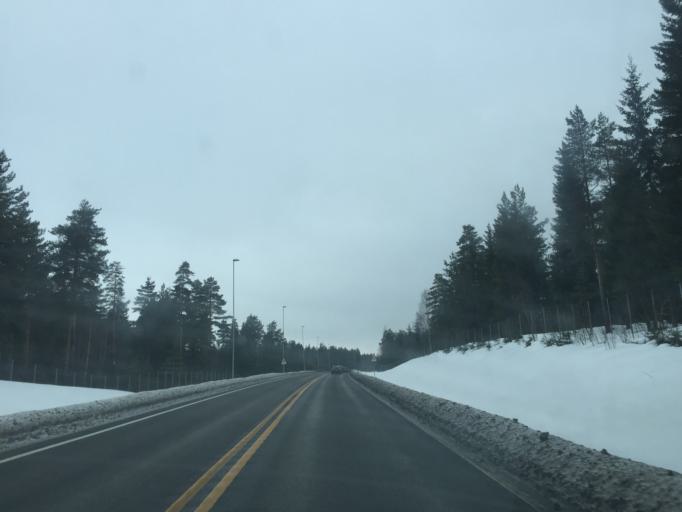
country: NO
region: Hedmark
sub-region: Loten
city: Loten
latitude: 60.7496
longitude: 11.3010
